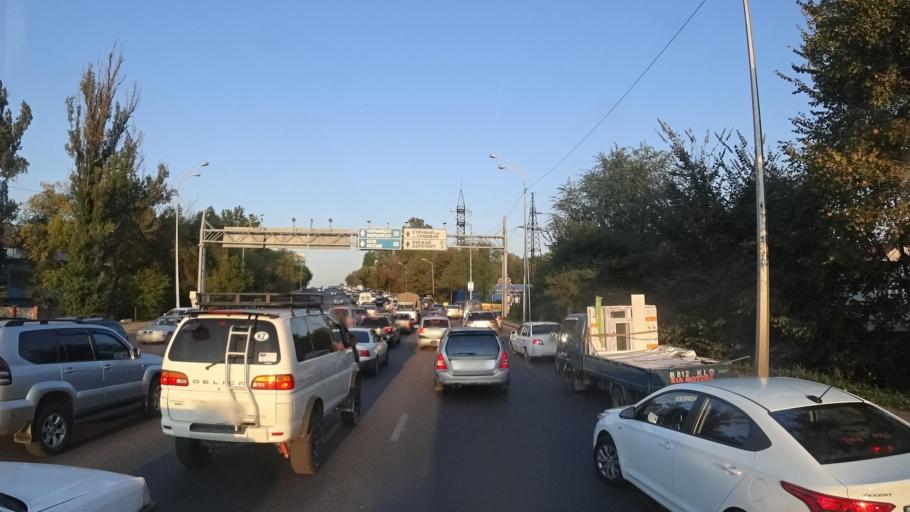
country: KZ
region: Almaty Qalasy
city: Almaty
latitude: 43.2932
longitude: 76.9437
